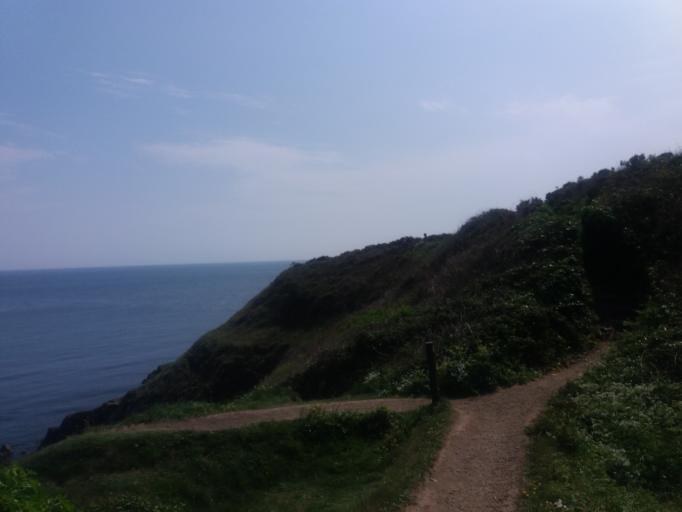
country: IE
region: Leinster
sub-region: Fingal County
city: Howth
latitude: 53.3611
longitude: -6.0756
